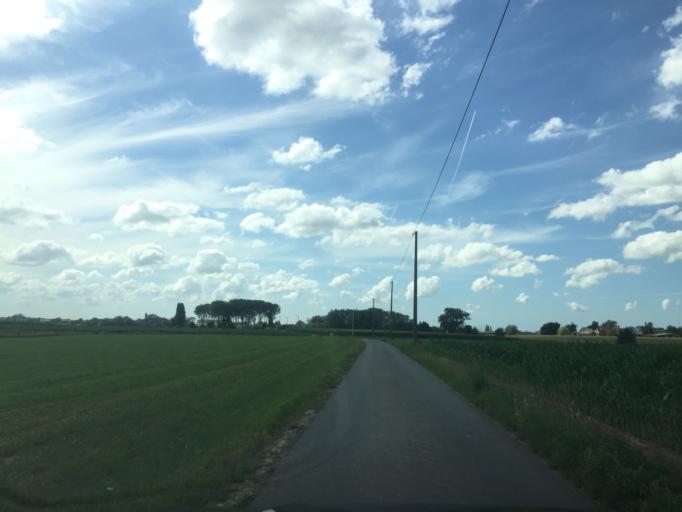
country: BE
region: Flanders
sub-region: Provincie West-Vlaanderen
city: Staden
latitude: 50.9849
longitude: 3.0385
